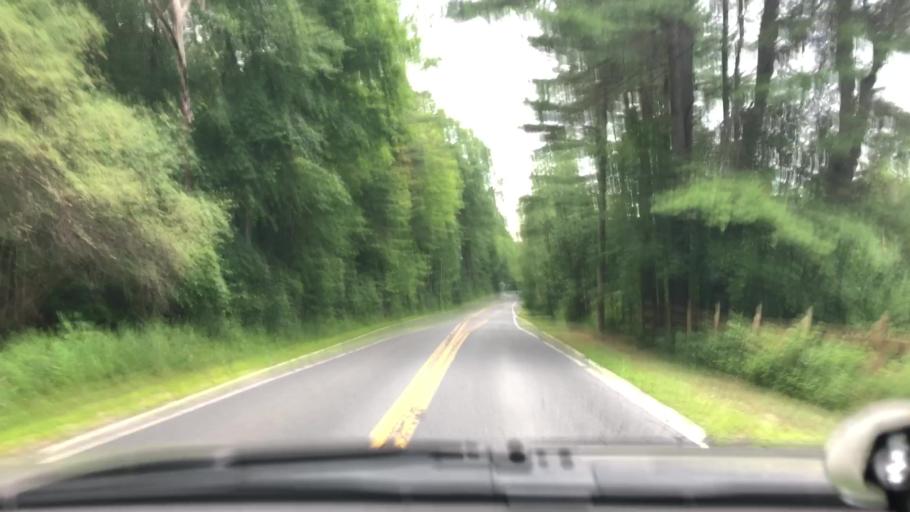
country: US
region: New York
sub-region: Saratoga County
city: Corinth
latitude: 43.2163
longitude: -73.8042
